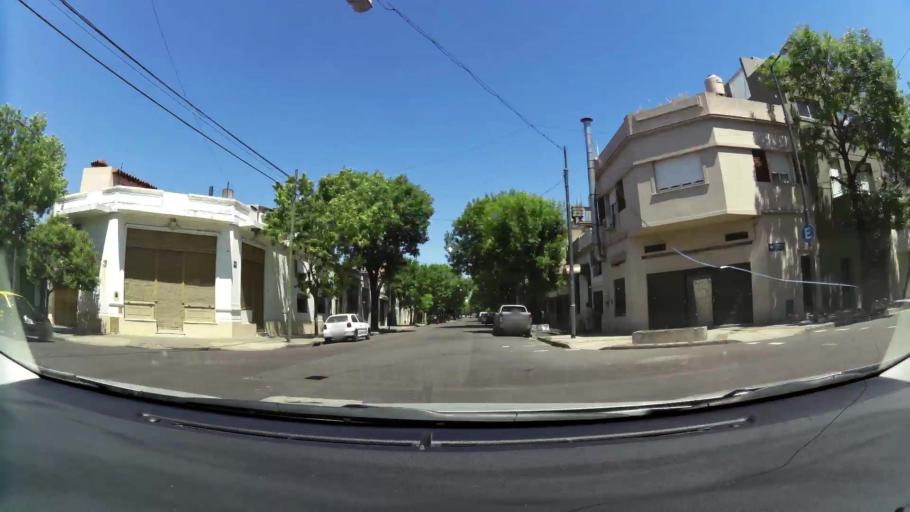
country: AR
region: Buenos Aires
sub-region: Partido de Avellaneda
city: Avellaneda
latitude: -34.6464
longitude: -58.4109
